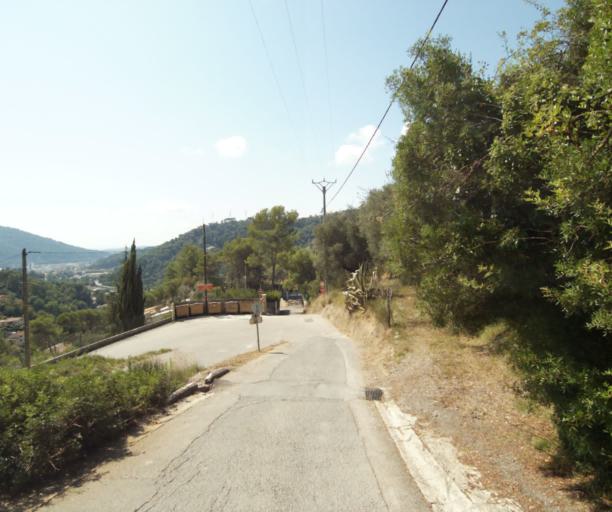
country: FR
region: Provence-Alpes-Cote d'Azur
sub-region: Departement des Alpes-Maritimes
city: Drap
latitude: 43.7546
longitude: 7.3268
